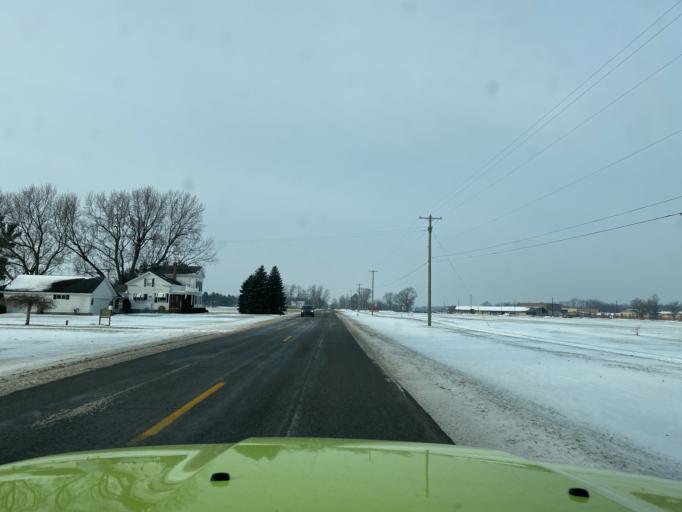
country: US
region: Michigan
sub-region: Ottawa County
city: Allendale
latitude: 42.9577
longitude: -85.9586
